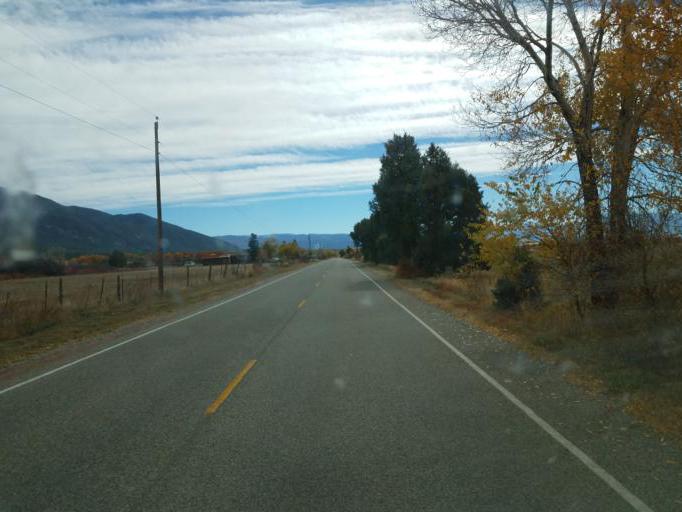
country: US
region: New Mexico
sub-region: Taos County
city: Arroyo Seco
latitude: 36.5271
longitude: -105.5713
